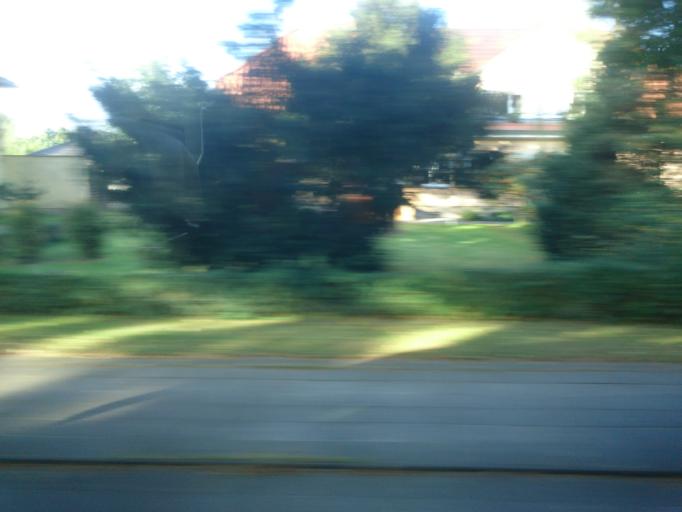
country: DE
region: Mecklenburg-Vorpommern
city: Anklam
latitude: 53.8451
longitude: 13.7099
